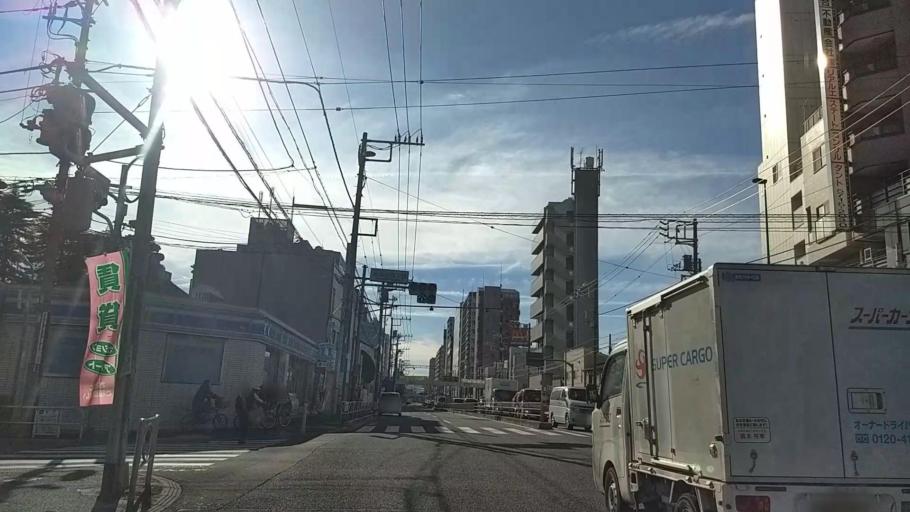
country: JP
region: Tokyo
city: Tokyo
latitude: 35.6146
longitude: 139.7413
